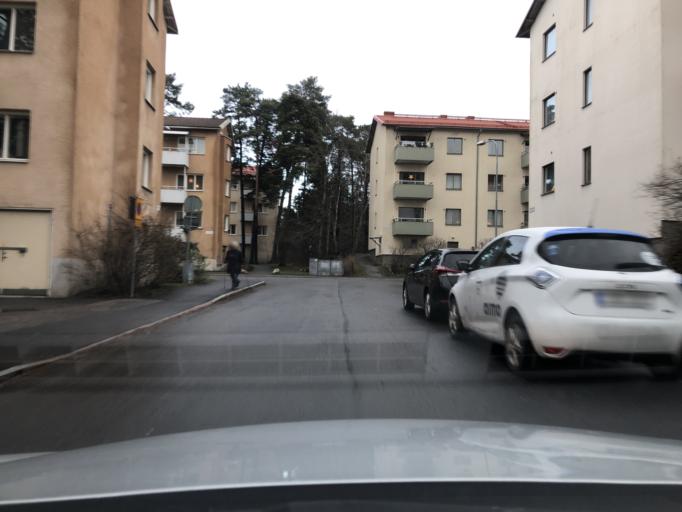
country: SE
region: Stockholm
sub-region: Stockholms Kommun
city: Arsta
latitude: 59.3002
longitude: 18.0550
